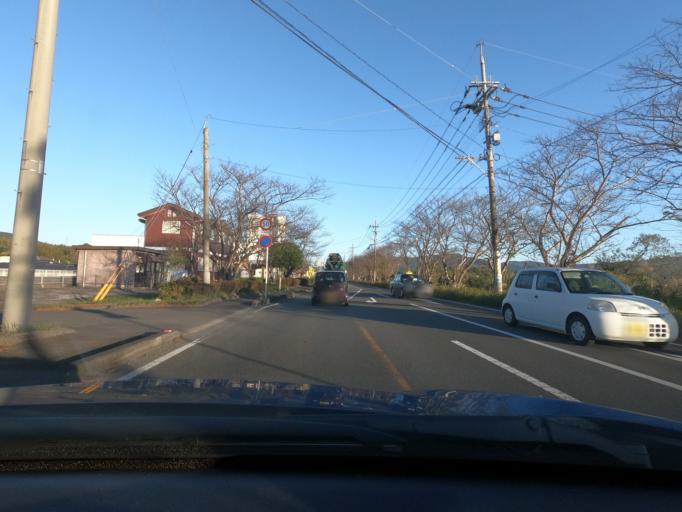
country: JP
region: Kagoshima
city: Satsumasendai
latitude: 31.8099
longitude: 130.3166
